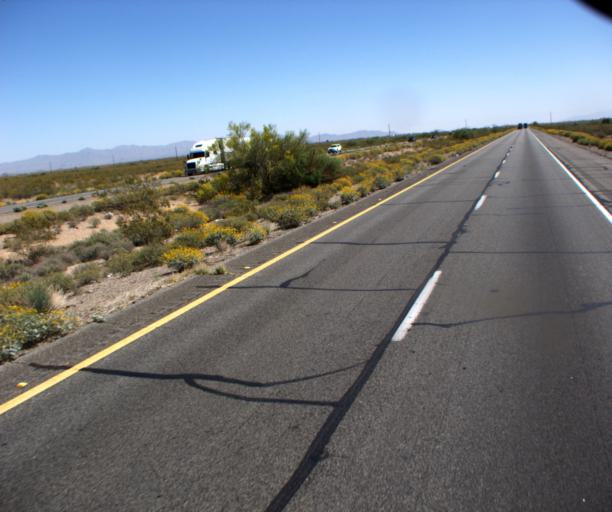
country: US
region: Arizona
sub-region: Maricopa County
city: Buckeye
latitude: 33.4758
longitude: -112.8412
